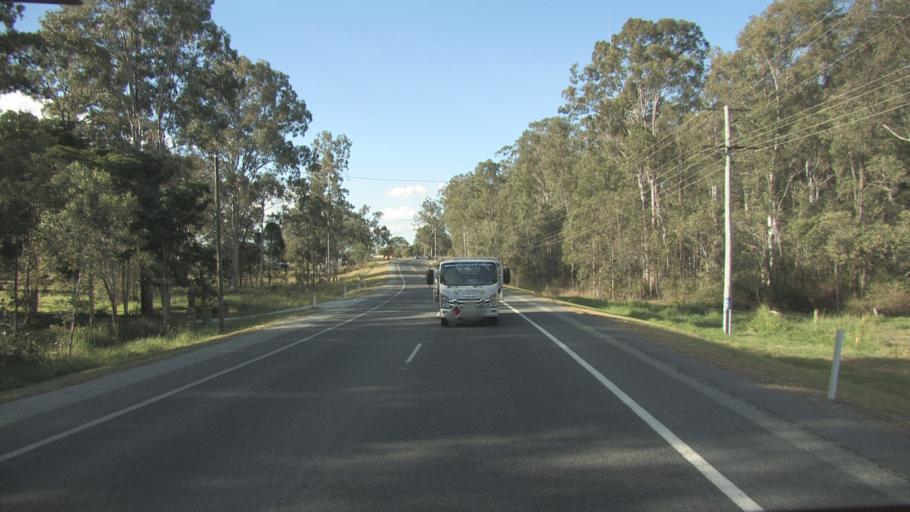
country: AU
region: Queensland
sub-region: Ipswich
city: Springfield Lakes
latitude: -27.7223
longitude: 152.9605
